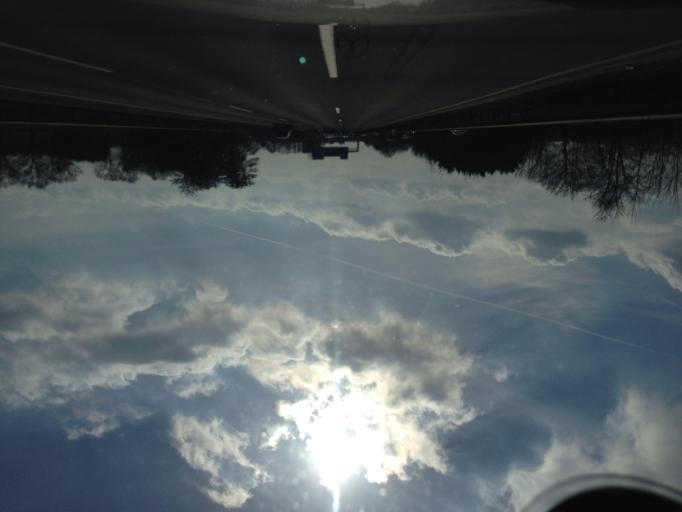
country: DE
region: Lower Saxony
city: Seevetal
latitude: 53.4096
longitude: 10.0287
